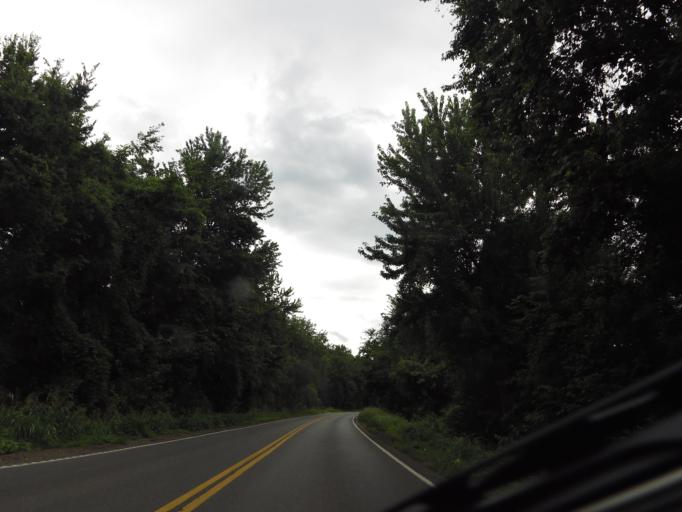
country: US
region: Kentucky
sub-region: Ballard County
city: Wickliffe
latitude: 36.9975
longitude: -89.1218
